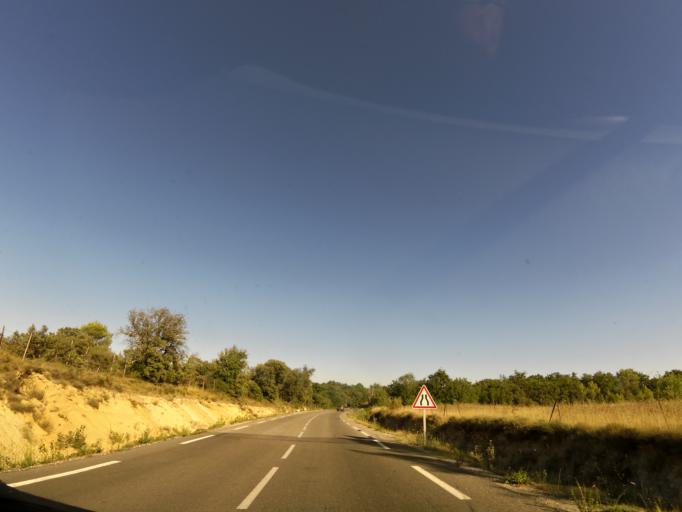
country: FR
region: Languedoc-Roussillon
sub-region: Departement du Gard
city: Quissac
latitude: 43.8799
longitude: 4.0079
